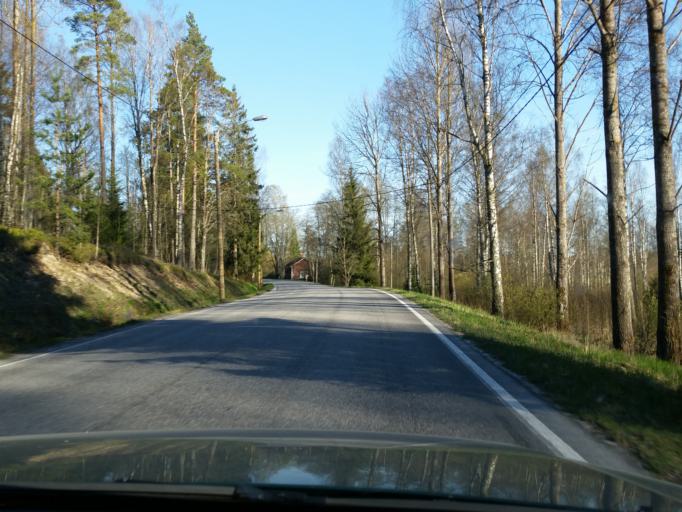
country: FI
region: Uusimaa
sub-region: Helsinki
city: Kirkkonummi
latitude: 60.1228
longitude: 24.5260
